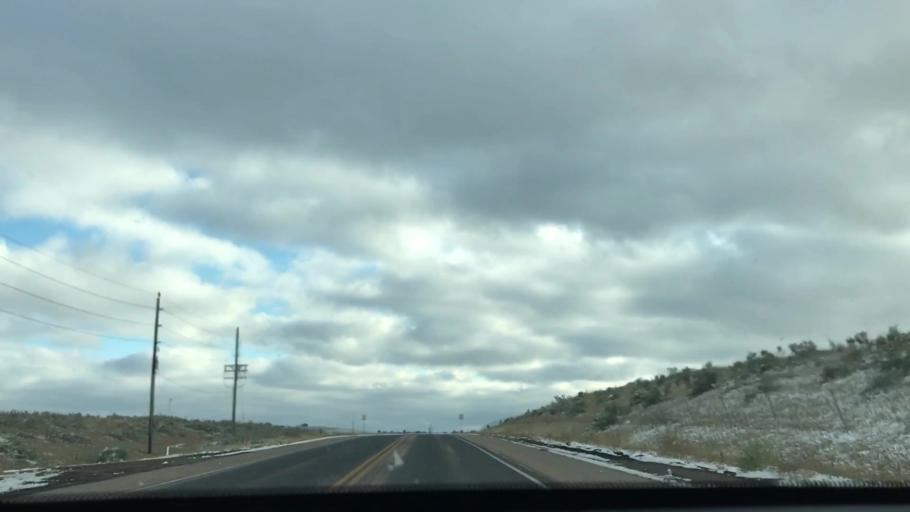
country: US
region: Colorado
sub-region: Boulder County
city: Lafayette
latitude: 39.9699
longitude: -105.0719
